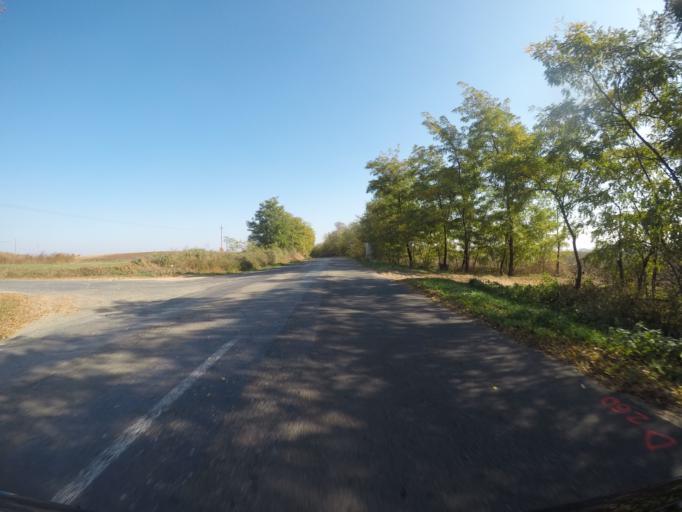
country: HU
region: Tolna
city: Tengelic
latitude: 46.6003
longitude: 18.7622
